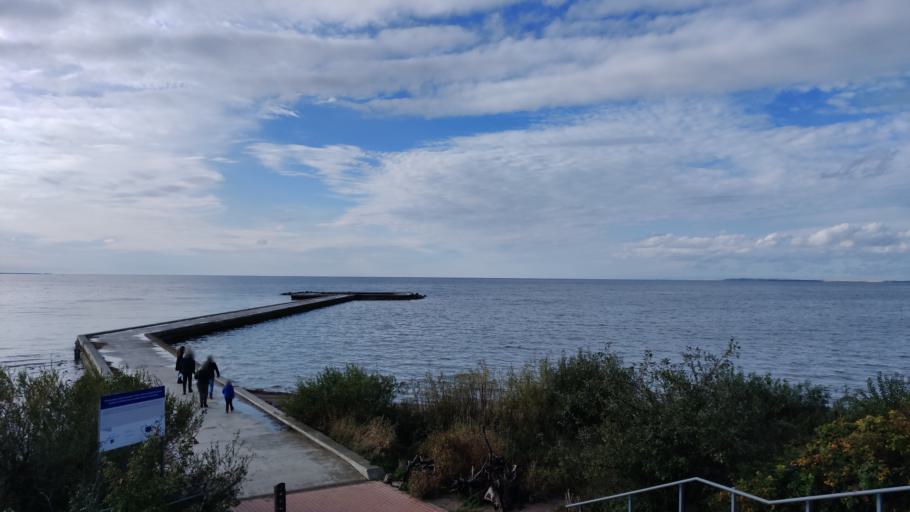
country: LT
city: Neringa
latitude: 55.3408
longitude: 21.1899
